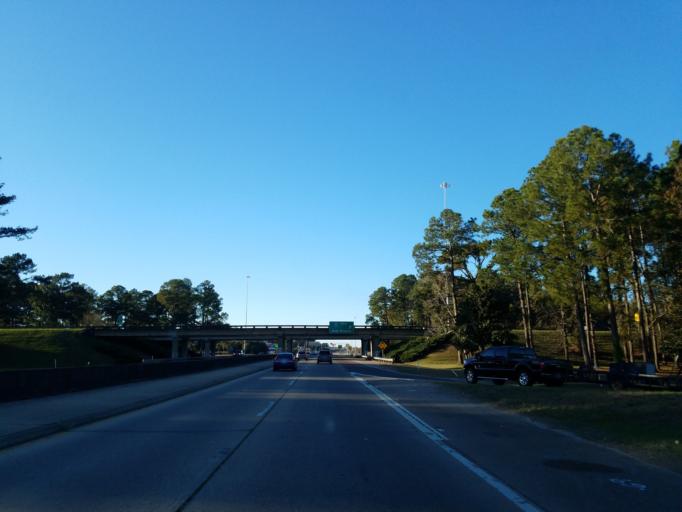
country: US
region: Mississippi
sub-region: Lamar County
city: Arnold Line
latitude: 31.3560
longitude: -89.3455
